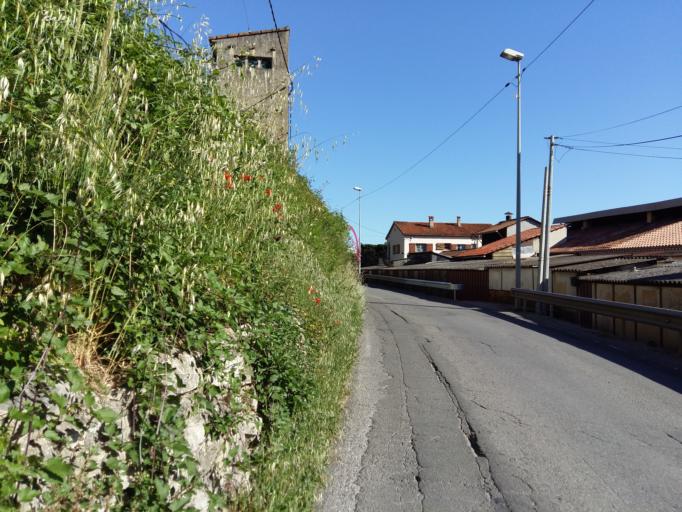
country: FR
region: Provence-Alpes-Cote d'Azur
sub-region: Departement des Alpes-Maritimes
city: Biot
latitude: 43.6267
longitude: 7.1024
